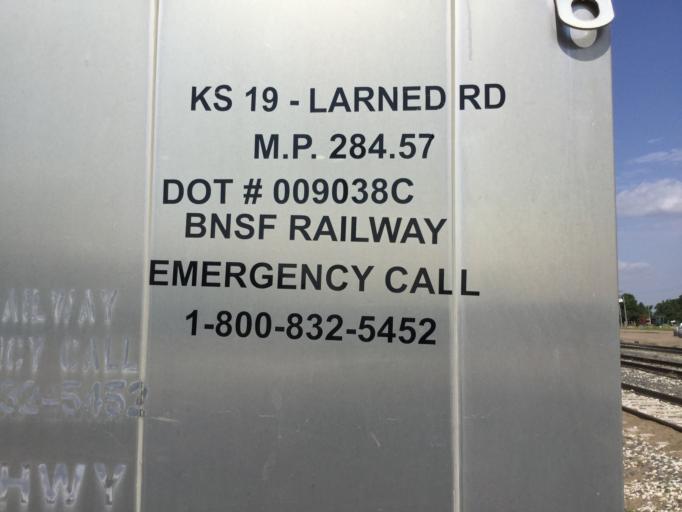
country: US
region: Kansas
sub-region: Pawnee County
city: Larned
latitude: 37.9530
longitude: -99.0957
